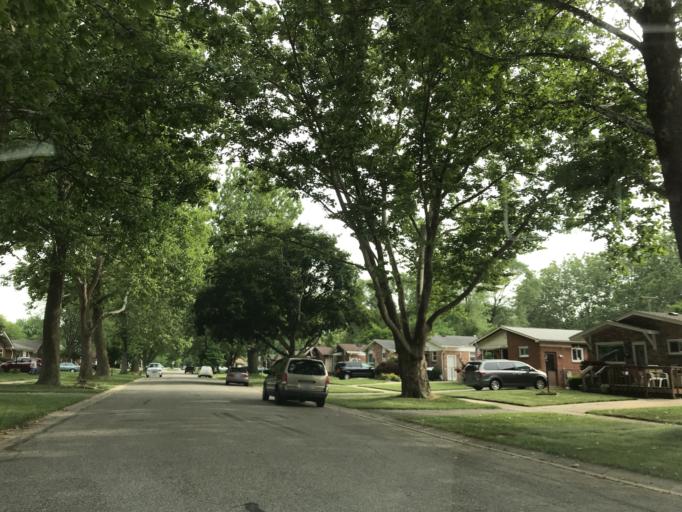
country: US
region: Michigan
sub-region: Wayne County
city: Redford
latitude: 42.4329
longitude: -83.3189
